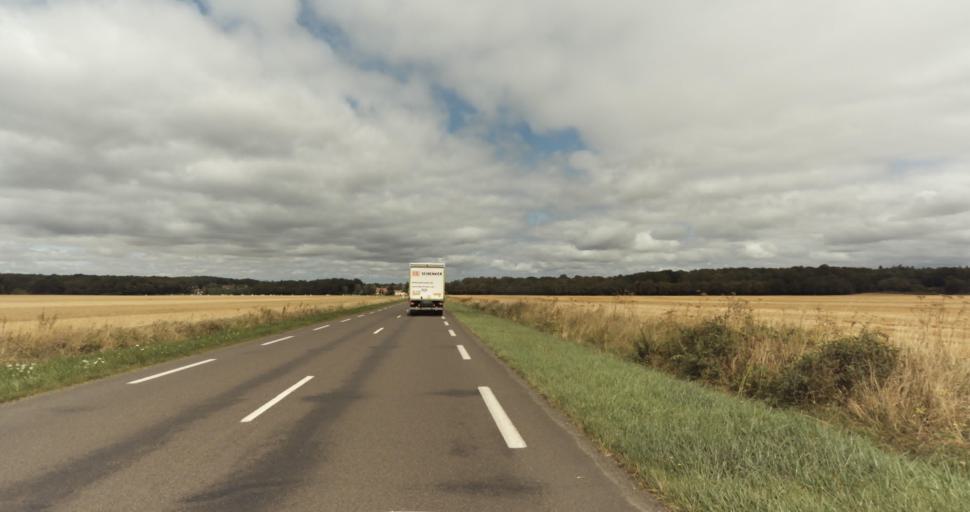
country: FR
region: Haute-Normandie
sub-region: Departement de l'Eure
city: Evreux
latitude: 48.9647
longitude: 1.1605
